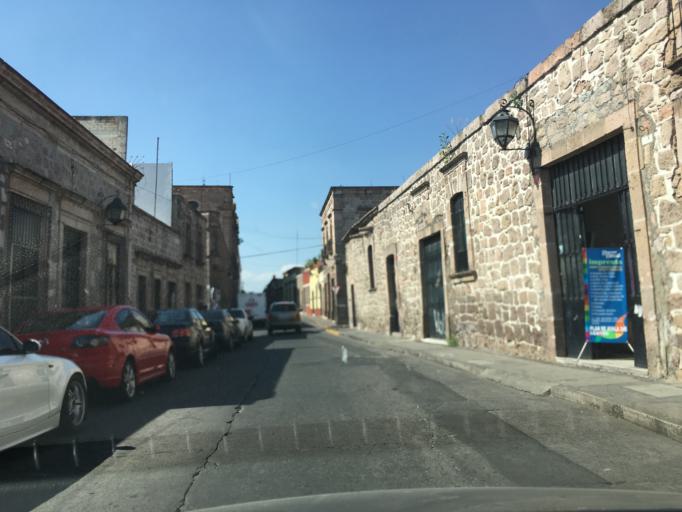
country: MX
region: Michoacan
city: Morelia
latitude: 19.7057
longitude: -101.1869
